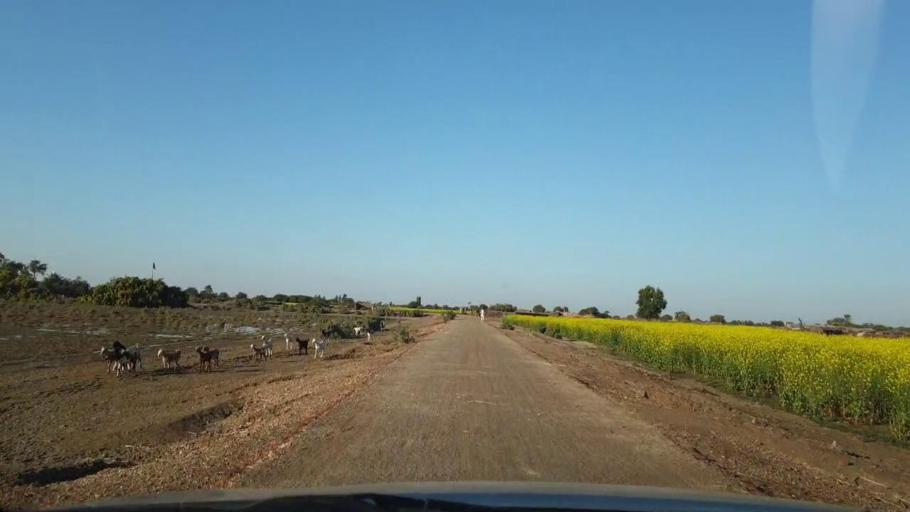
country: PK
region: Sindh
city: Jhol
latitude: 25.9168
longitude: 68.9265
